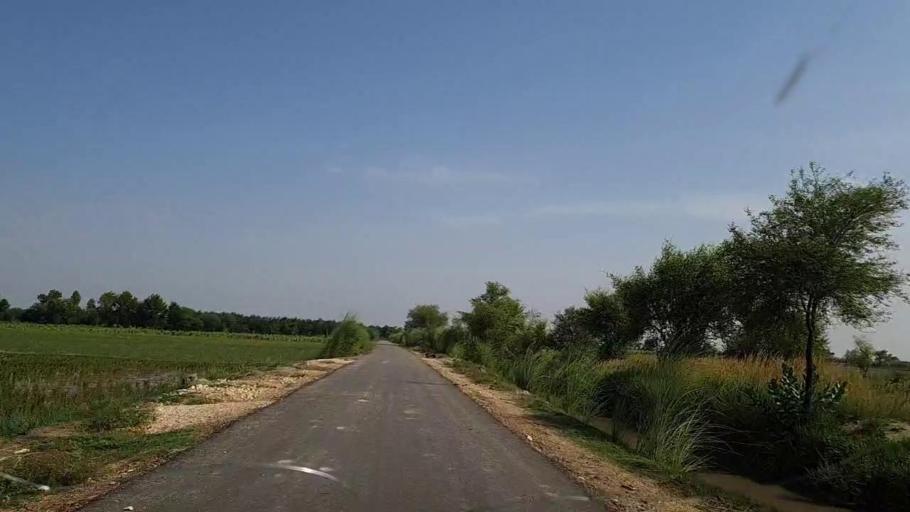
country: PK
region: Sindh
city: Khanpur
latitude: 27.6973
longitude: 69.3650
